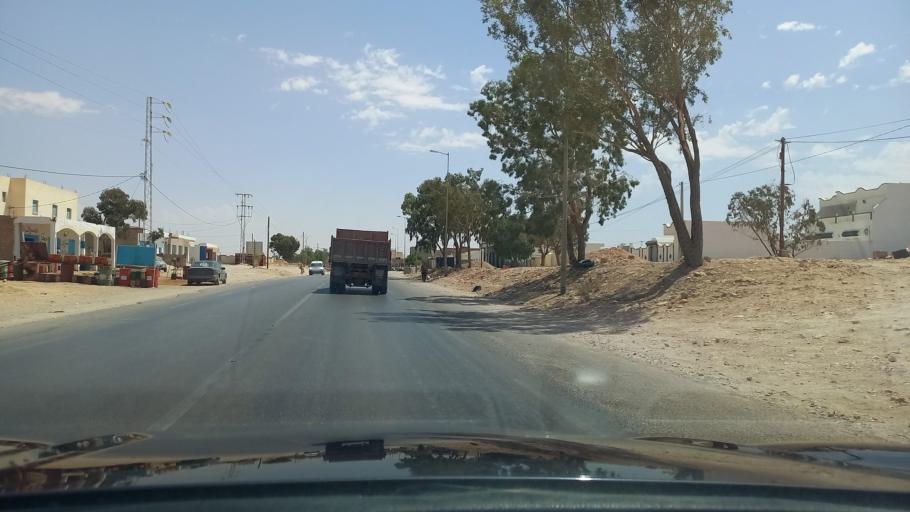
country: TN
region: Madanin
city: Medenine
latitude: 33.3718
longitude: 10.4477
